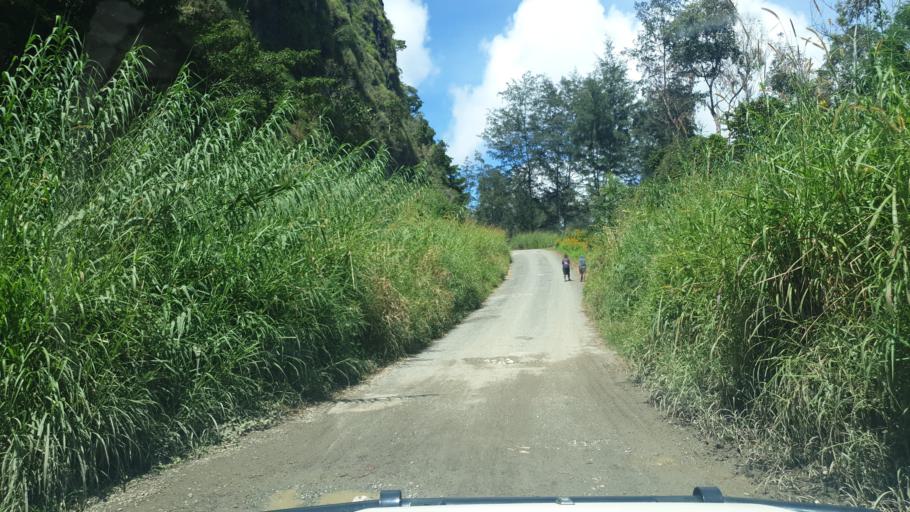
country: PG
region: Chimbu
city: Kundiawa
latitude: -6.1483
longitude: 145.1342
